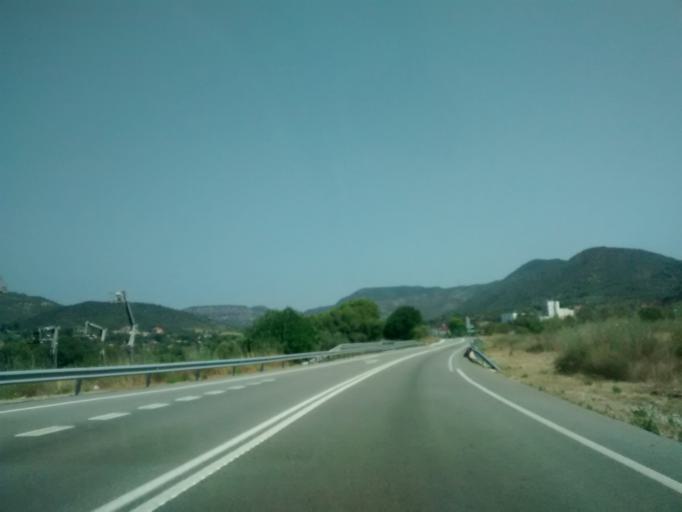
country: ES
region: Catalonia
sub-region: Provincia de Barcelona
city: Olesa de Montserrat
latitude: 41.5469
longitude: 1.8809
